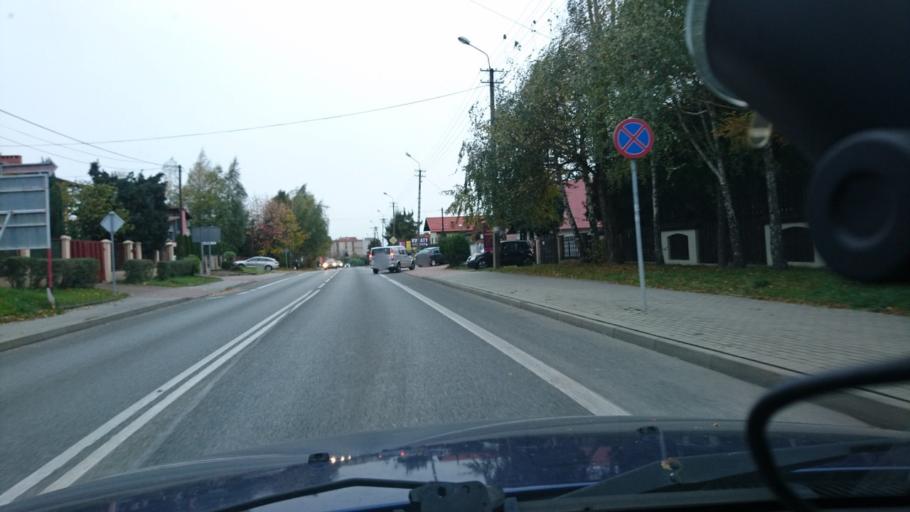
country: PL
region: Silesian Voivodeship
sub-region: Bielsko-Biala
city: Bielsko-Biala
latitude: 49.8092
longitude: 19.0167
